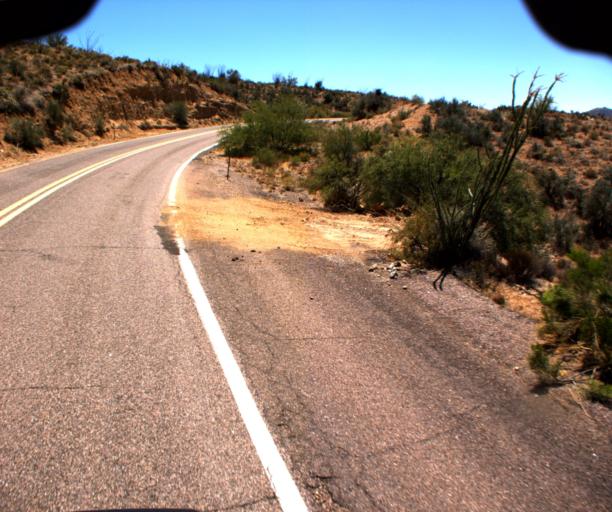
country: US
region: Arizona
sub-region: Yavapai County
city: Bagdad
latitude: 34.4601
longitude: -112.9975
